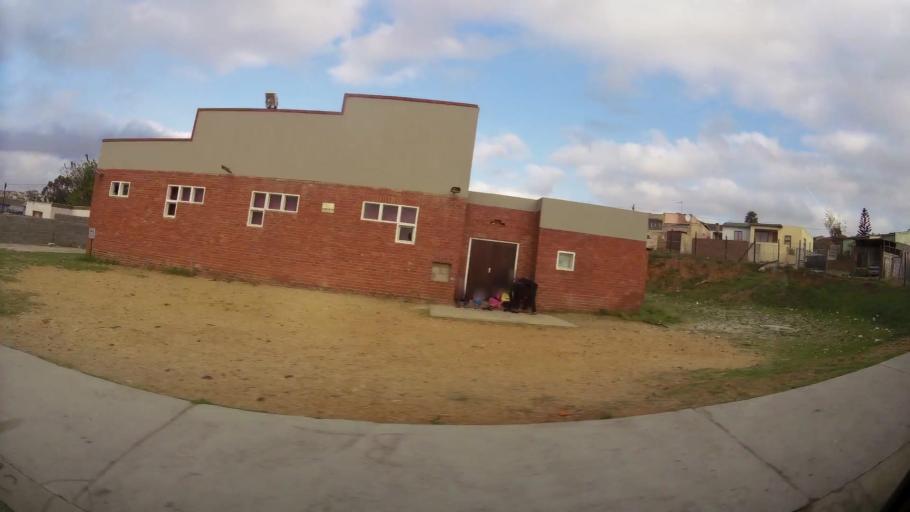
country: ZA
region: Eastern Cape
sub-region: Nelson Mandela Bay Metropolitan Municipality
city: Port Elizabeth
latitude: -33.9135
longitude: 25.5461
